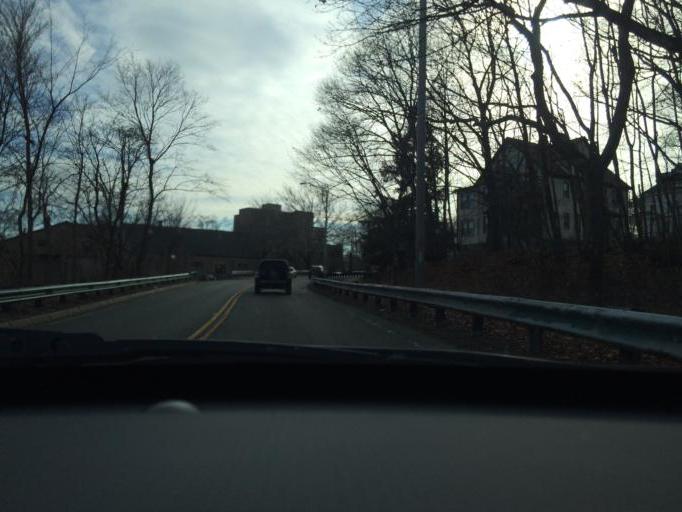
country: US
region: Massachusetts
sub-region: Norfolk County
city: Quincy
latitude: 42.2598
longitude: -71.0084
